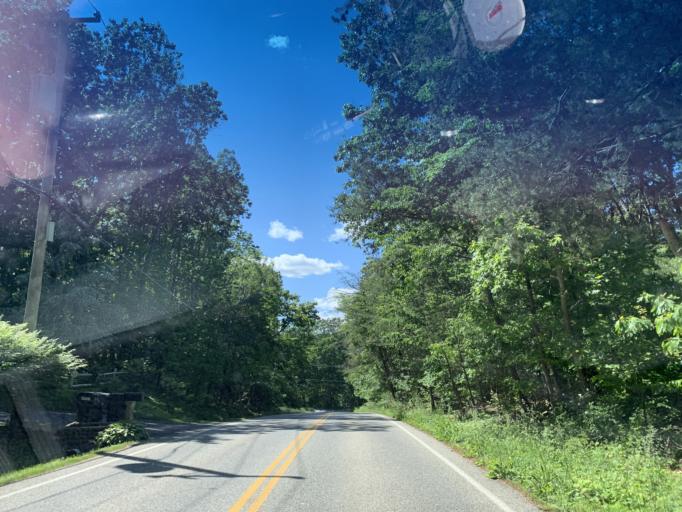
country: US
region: Maryland
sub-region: Cecil County
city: North East
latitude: 39.5622
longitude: -75.8876
